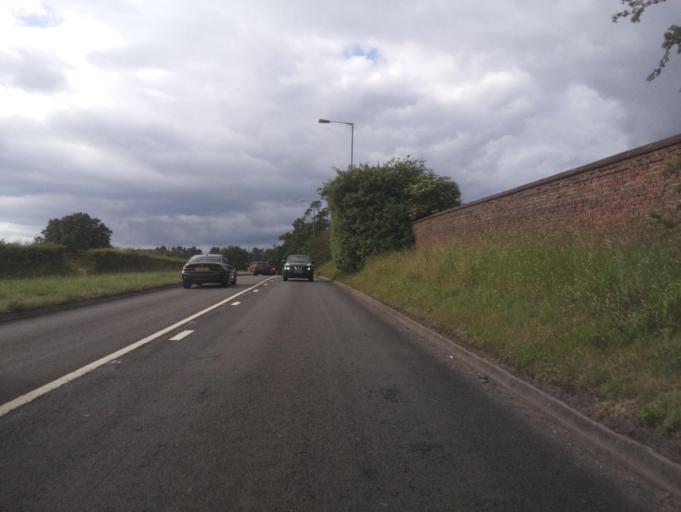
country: GB
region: England
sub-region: Dudley
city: Kingswinford
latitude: 52.5244
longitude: -2.1769
